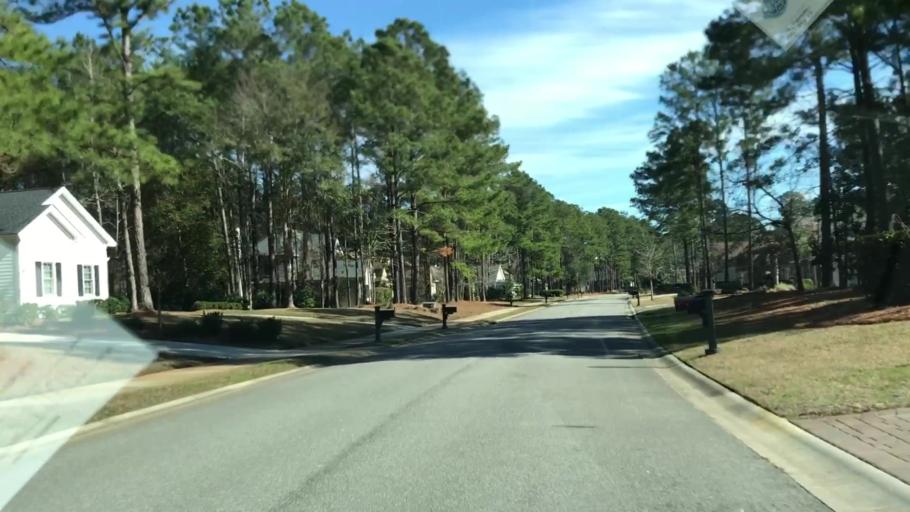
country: US
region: South Carolina
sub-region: Beaufort County
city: Bluffton
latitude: 32.2530
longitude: -80.9252
